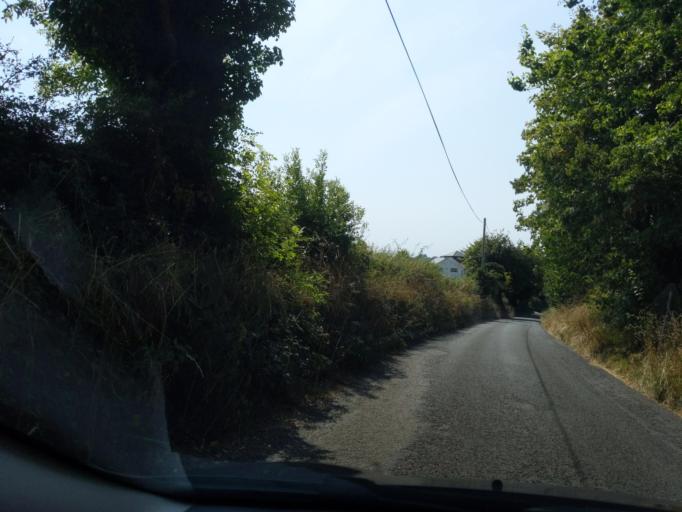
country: GB
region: England
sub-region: Cornwall
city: Fowey
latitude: 50.3435
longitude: -4.6248
